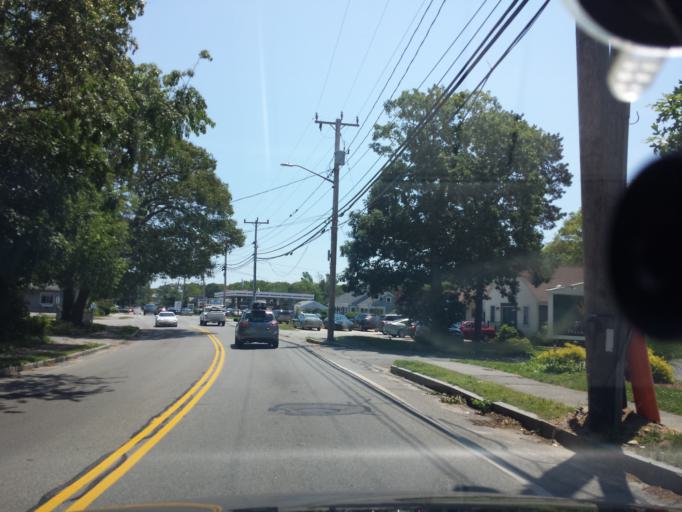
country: US
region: Massachusetts
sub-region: Barnstable County
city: Hyannis
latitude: 41.6496
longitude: -70.3125
